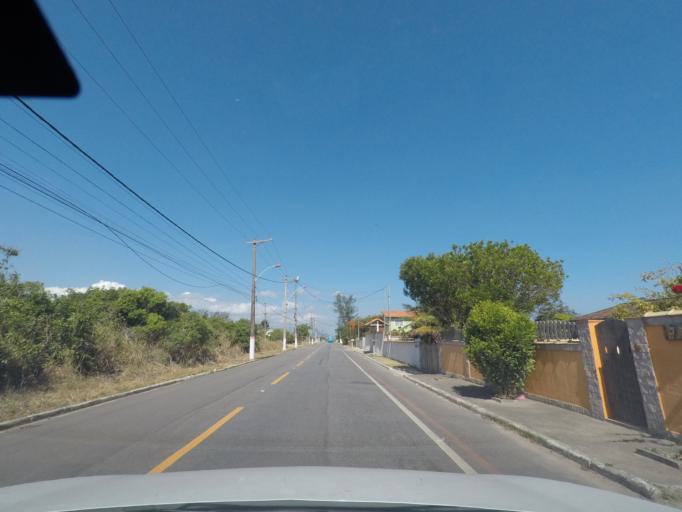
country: BR
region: Rio de Janeiro
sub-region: Marica
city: Marica
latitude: -22.9692
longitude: -42.9080
